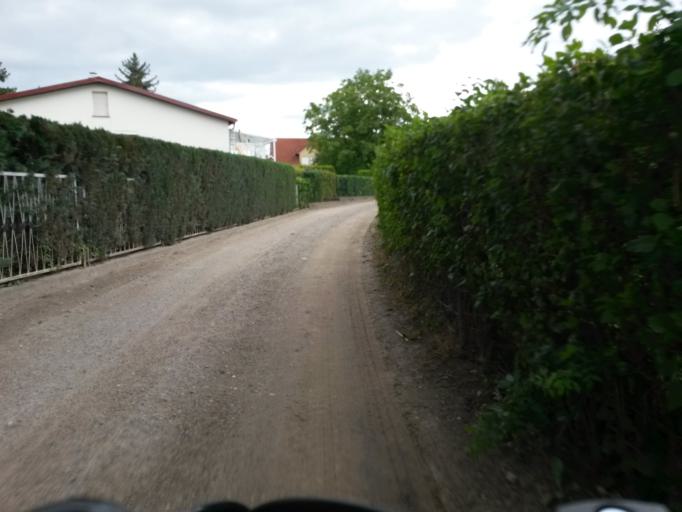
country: DE
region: Brandenburg
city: Angermunde
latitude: 53.0144
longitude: 14.0061
